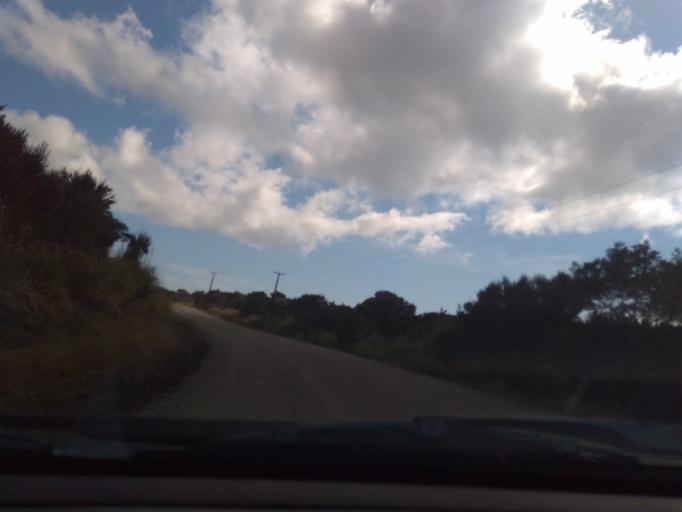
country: NZ
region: Northland
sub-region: Far North District
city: Taipa
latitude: -34.9499
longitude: 173.3772
